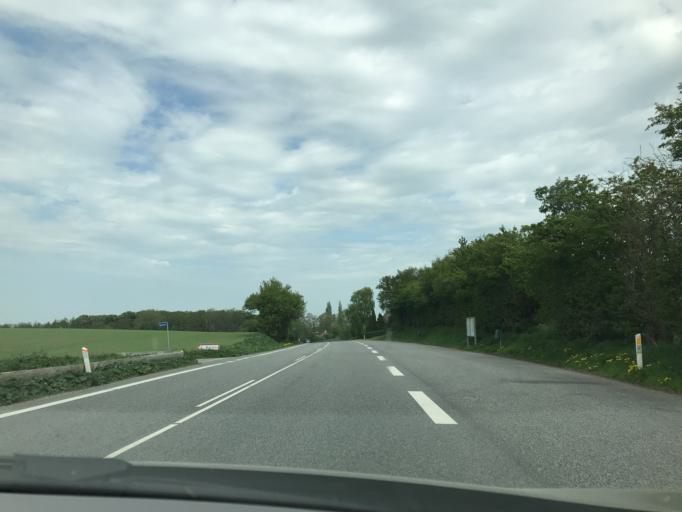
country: DK
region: South Denmark
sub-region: Assens Kommune
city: Assens
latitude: 55.3041
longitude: 9.9440
